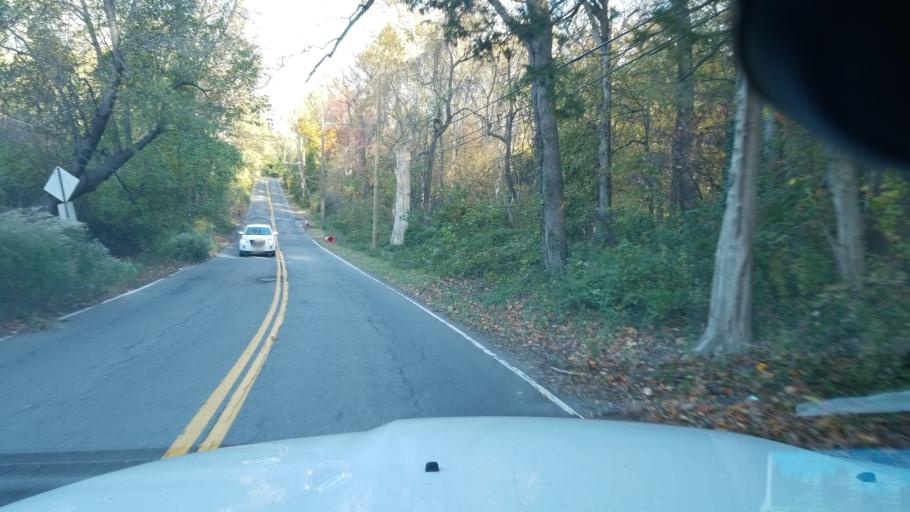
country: US
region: Maryland
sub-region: Montgomery County
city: Chevy Chase
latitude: 38.9636
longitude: -77.0531
